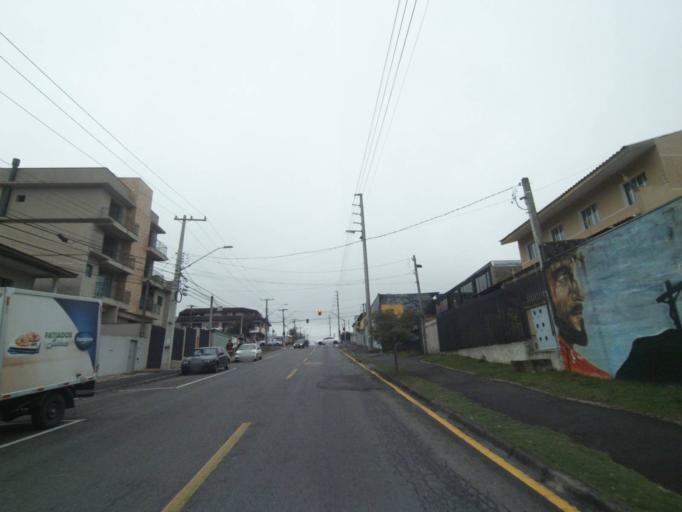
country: BR
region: Parana
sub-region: Curitiba
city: Curitiba
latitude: -25.5127
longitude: -49.3045
